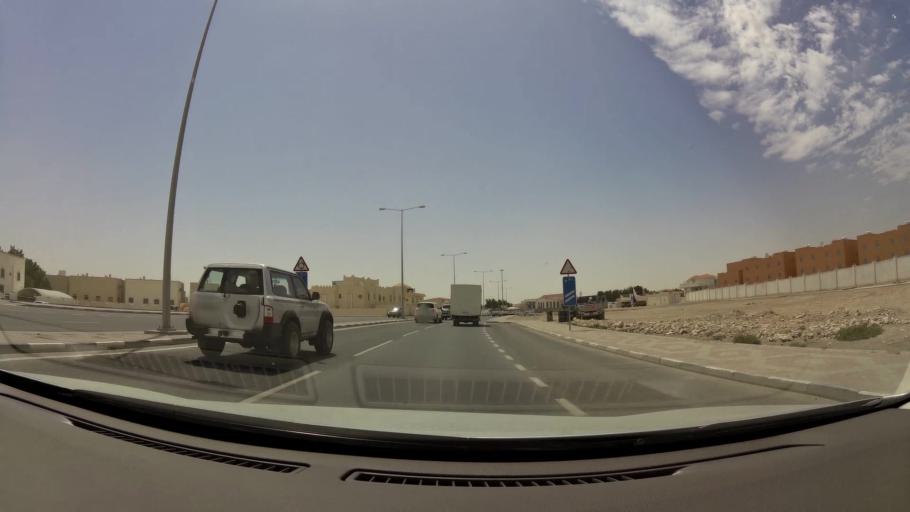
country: QA
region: Baladiyat ar Rayyan
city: Ar Rayyan
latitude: 25.2622
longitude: 51.4202
